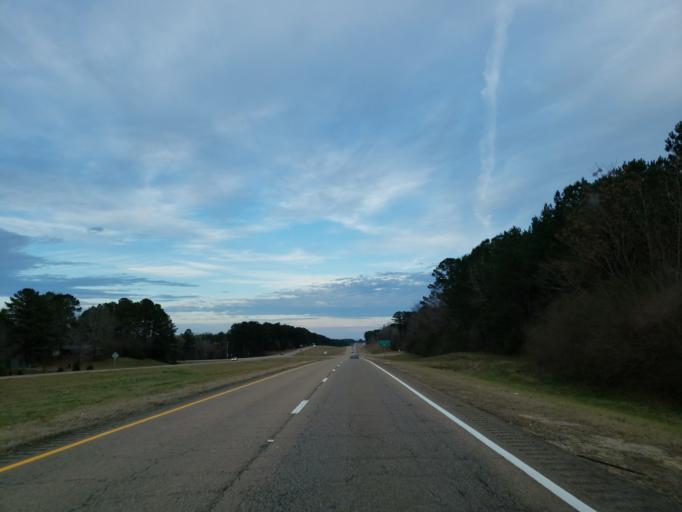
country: US
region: Mississippi
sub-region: Lauderdale County
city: Meridian Station
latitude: 32.4905
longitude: -88.5841
